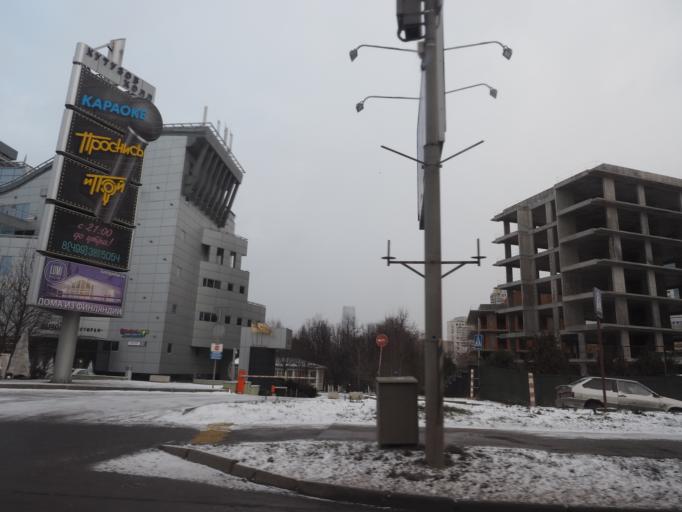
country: RU
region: Moskovskaya
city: Kastanayevo
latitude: 55.7176
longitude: 37.5023
